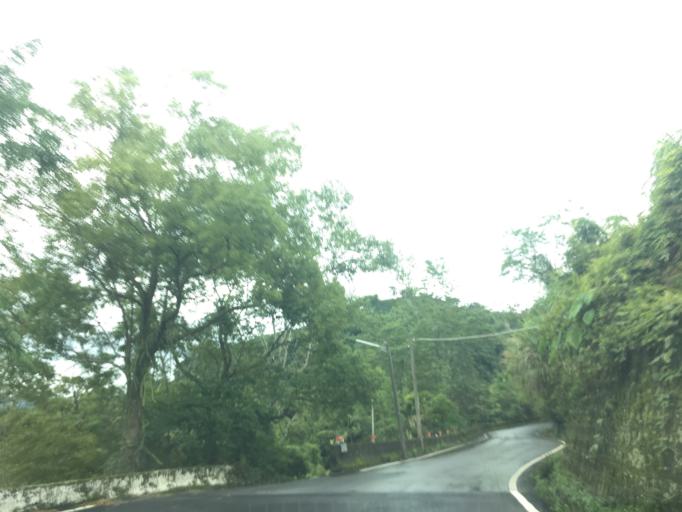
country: TW
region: Taiwan
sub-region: Yunlin
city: Douliu
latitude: 23.5633
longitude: 120.6554
